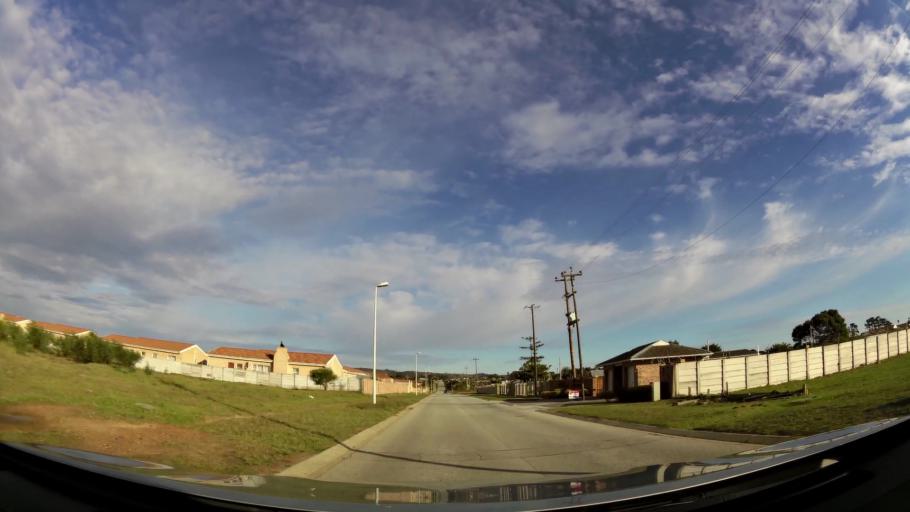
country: ZA
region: Eastern Cape
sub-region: Nelson Mandela Bay Metropolitan Municipality
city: Port Elizabeth
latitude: -33.9518
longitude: 25.4873
